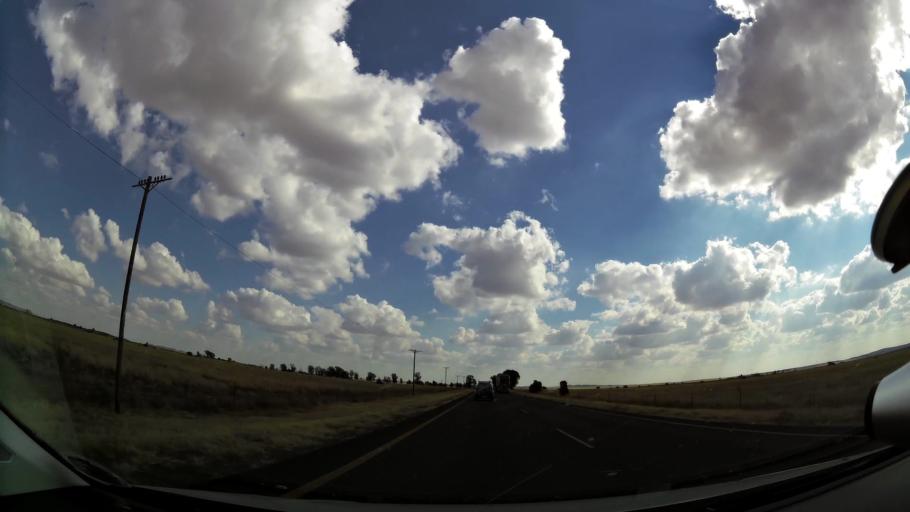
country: ZA
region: Orange Free State
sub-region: Xhariep District Municipality
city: Koffiefontein
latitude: -29.1317
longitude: 25.5331
